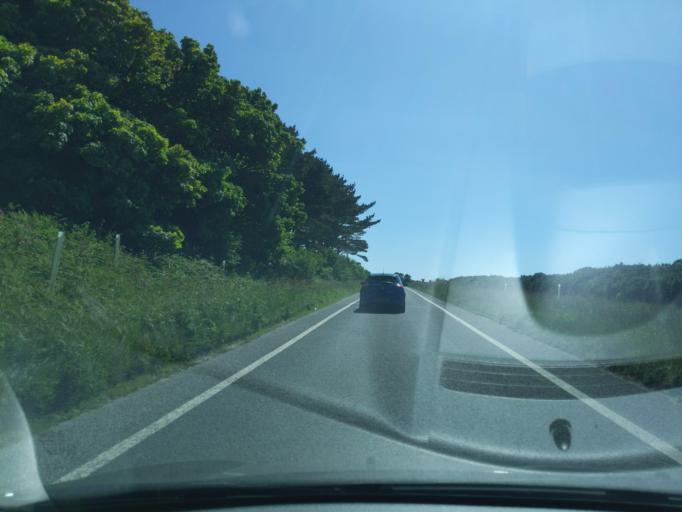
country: GB
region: England
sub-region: Cornwall
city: Penryn
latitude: 50.1689
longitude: -5.1477
